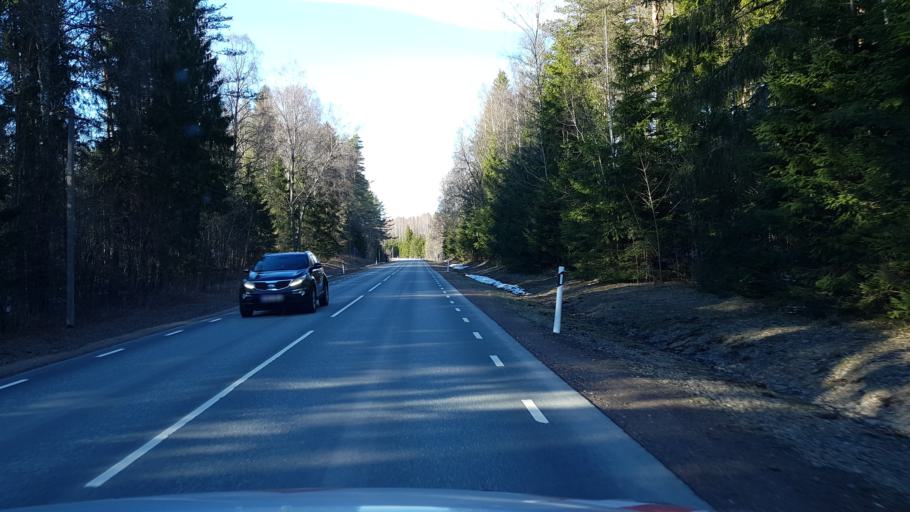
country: EE
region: Laeaene-Virumaa
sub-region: Kadrina vald
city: Kadrina
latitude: 59.3961
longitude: 26.0134
